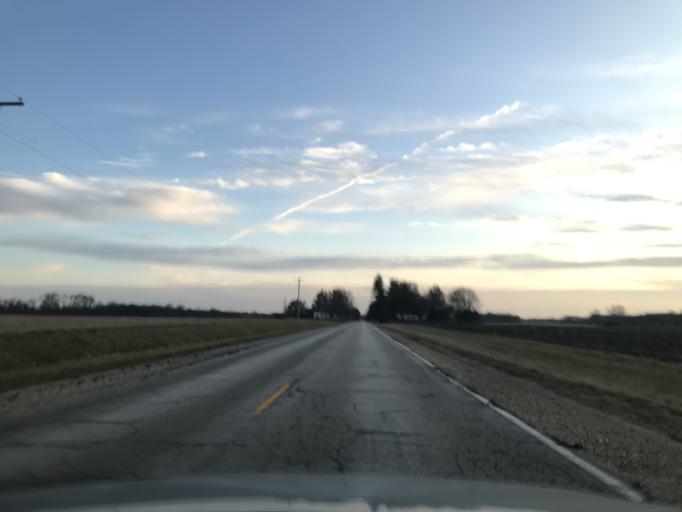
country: US
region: Illinois
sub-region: Henderson County
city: Oquawka
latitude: 40.9445
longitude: -90.8641
